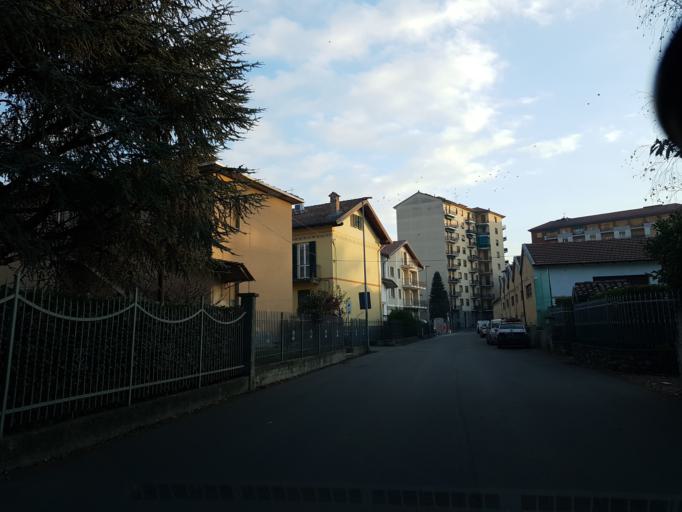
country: IT
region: Piedmont
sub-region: Provincia di Alessandria
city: Novi Ligure
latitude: 44.7678
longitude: 8.7942
